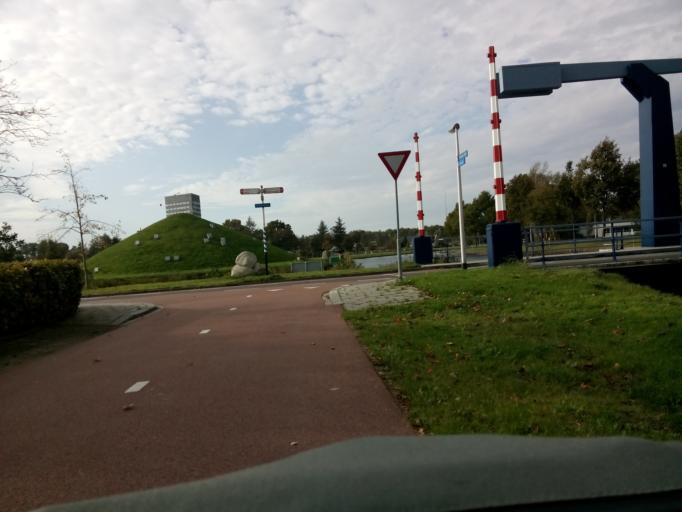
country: NL
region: Drenthe
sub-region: Gemeente Assen
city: Assen
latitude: 52.9989
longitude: 6.5316
